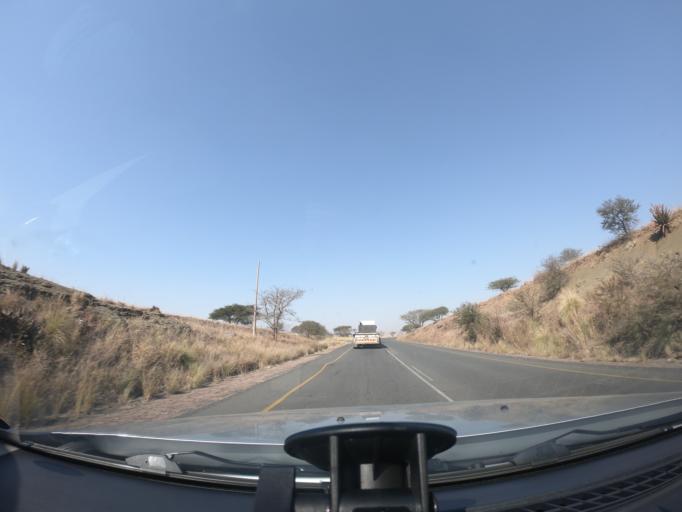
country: ZA
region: KwaZulu-Natal
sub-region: uThukela District Municipality
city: Ladysmith
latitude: -28.7511
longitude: 29.8224
